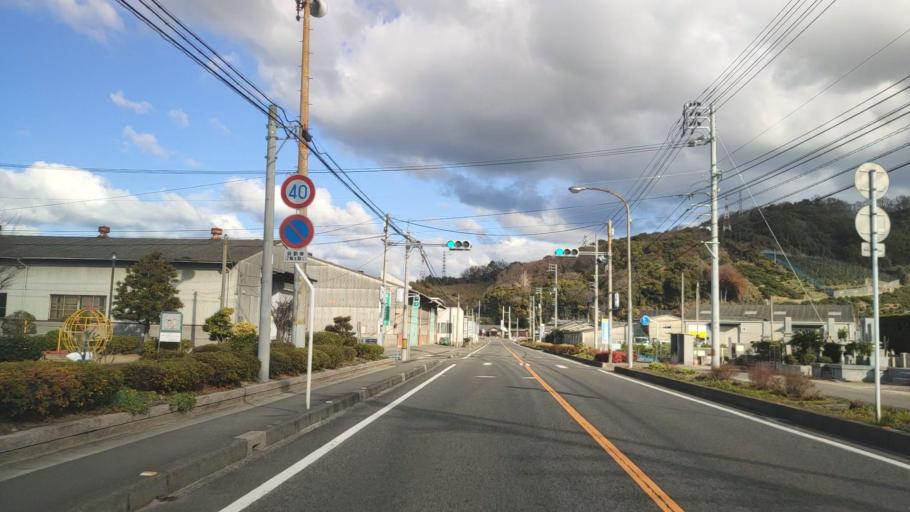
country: JP
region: Ehime
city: Masaki-cho
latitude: 33.8380
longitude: 132.7092
